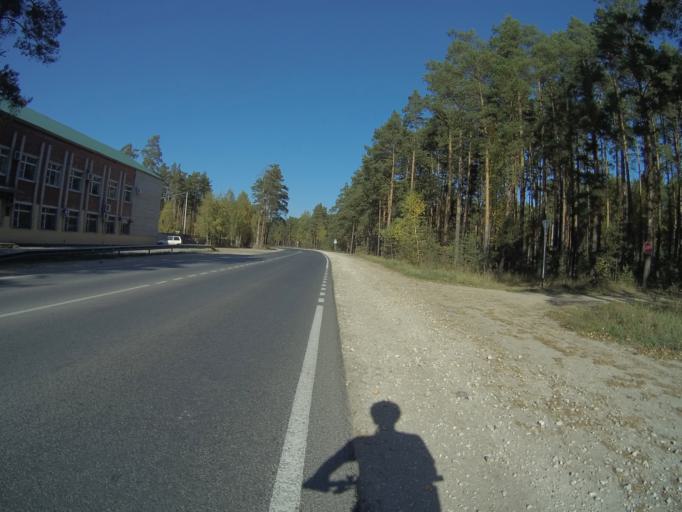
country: RU
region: Vladimir
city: Raduzhnyy
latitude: 56.0272
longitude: 40.3796
